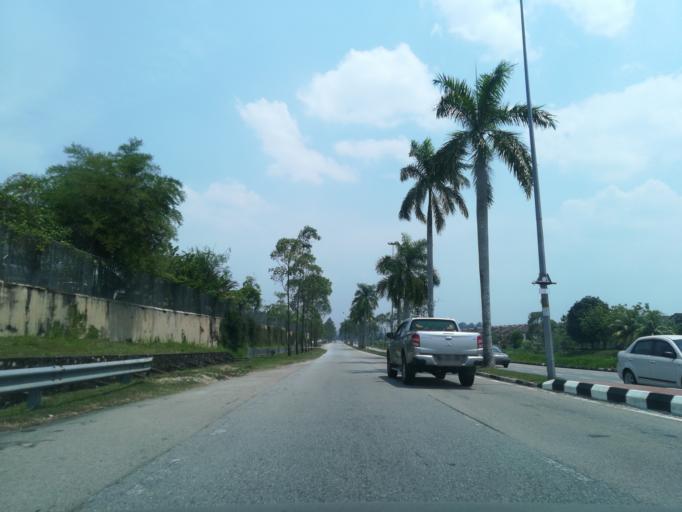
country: MY
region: Kedah
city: Kulim
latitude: 5.4000
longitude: 100.5758
